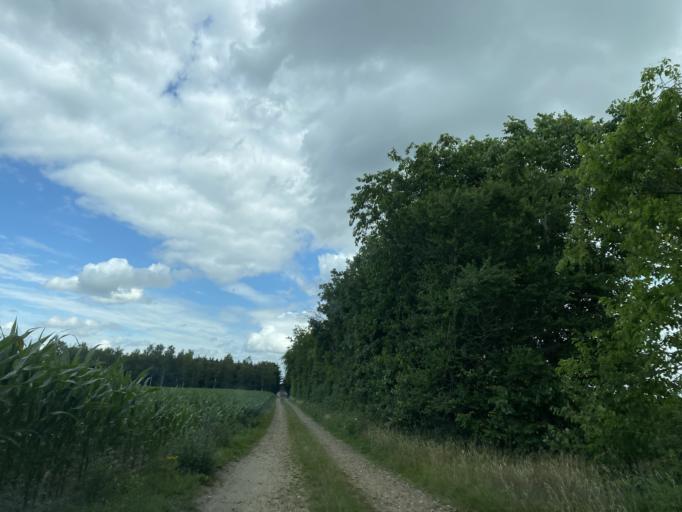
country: DK
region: Central Jutland
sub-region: Viborg Kommune
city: Bjerringbro
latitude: 56.2824
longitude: 9.6580
